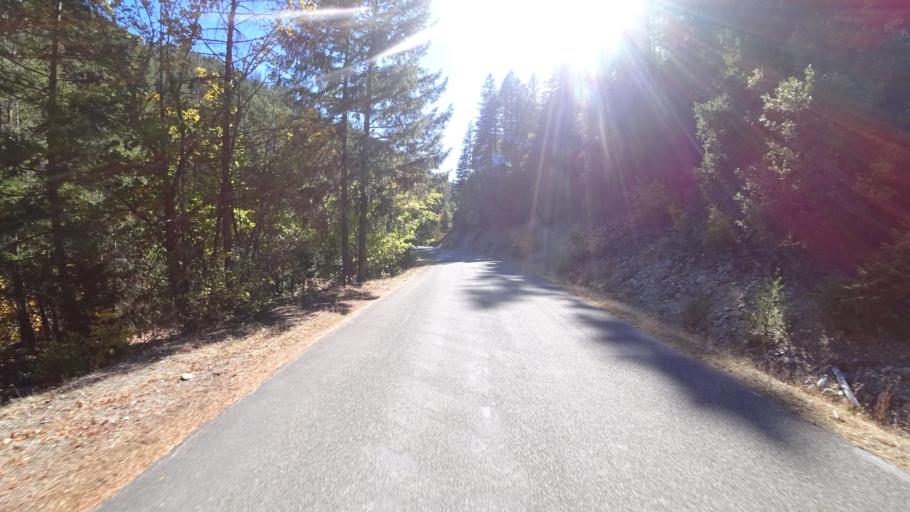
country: US
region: California
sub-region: Siskiyou County
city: Happy Camp
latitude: 41.3453
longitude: -123.0431
